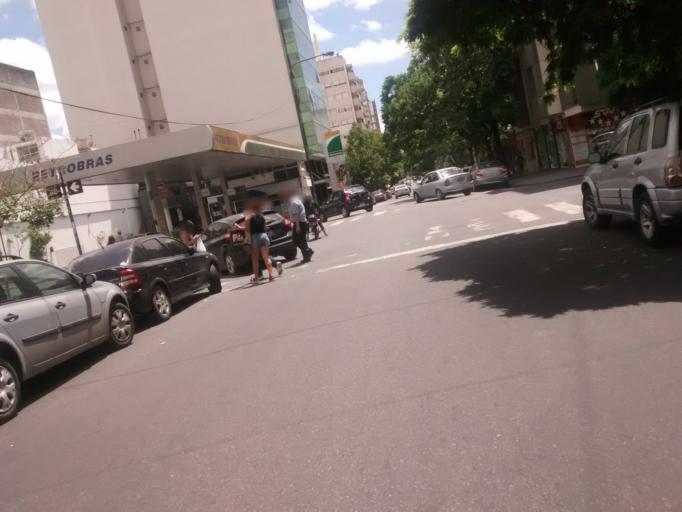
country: AR
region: Buenos Aires
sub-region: Partido de La Plata
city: La Plata
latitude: -34.9185
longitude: -57.9561
